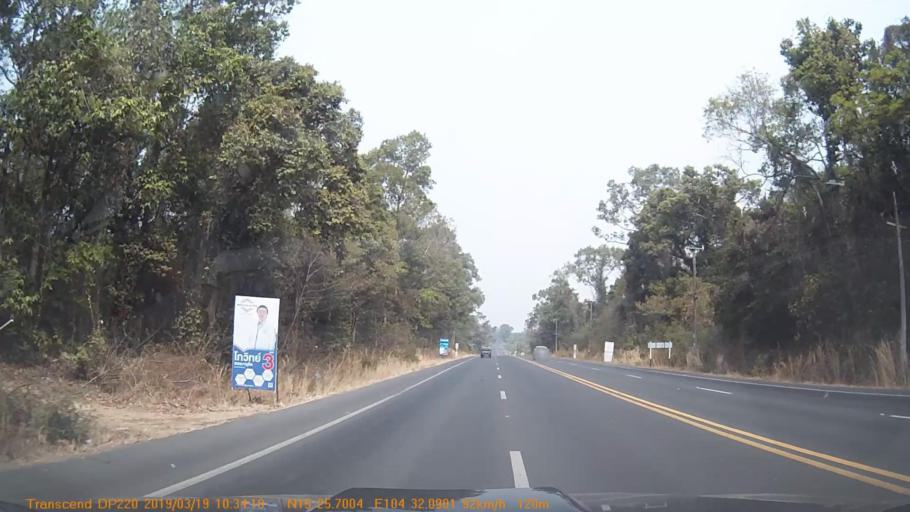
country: TH
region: Changwat Ubon Ratchathani
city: Khueang Nai
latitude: 15.4287
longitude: 104.5346
